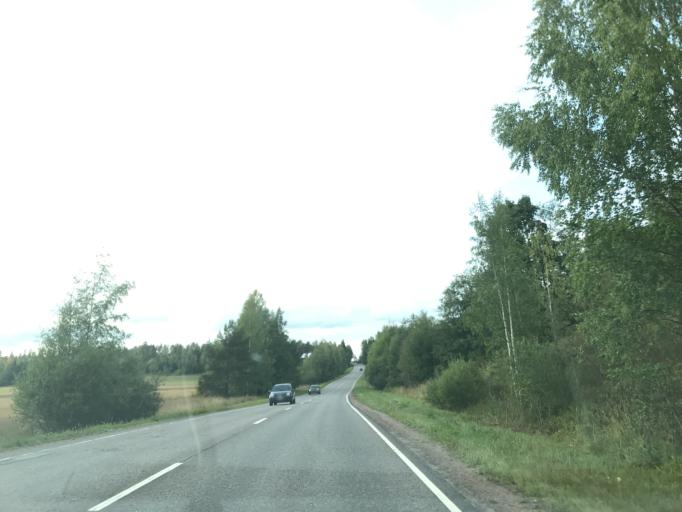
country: FI
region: Uusimaa
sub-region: Helsinki
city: Espoo
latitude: 60.1949
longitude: 24.5622
